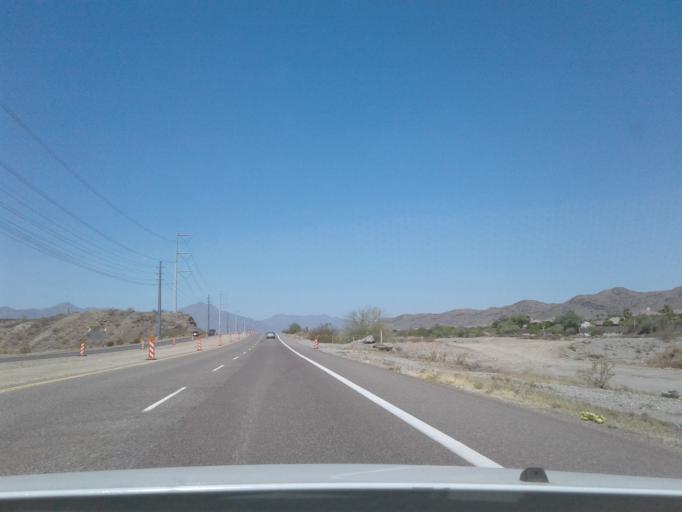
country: US
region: Arizona
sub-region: Maricopa County
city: Laveen
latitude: 33.2911
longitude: -112.0860
